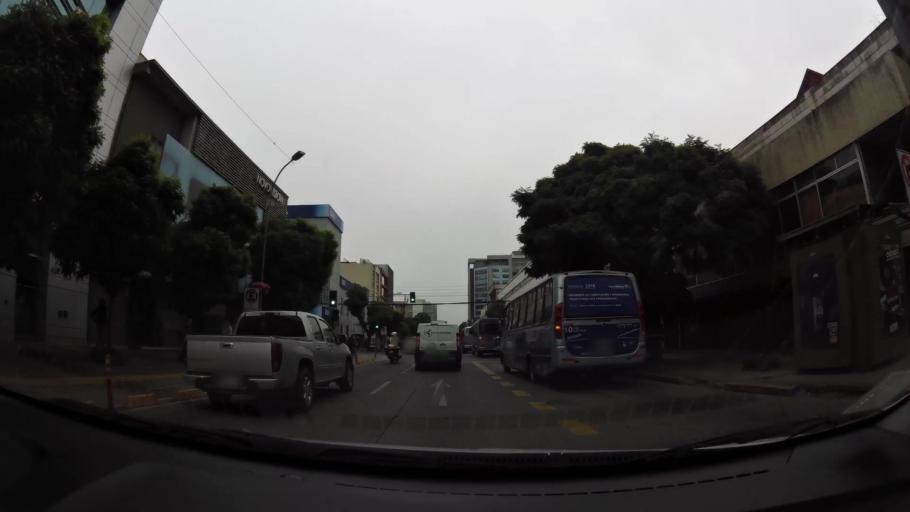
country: CL
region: Biobio
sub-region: Provincia de Concepcion
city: Concepcion
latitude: -36.8287
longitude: -73.0527
